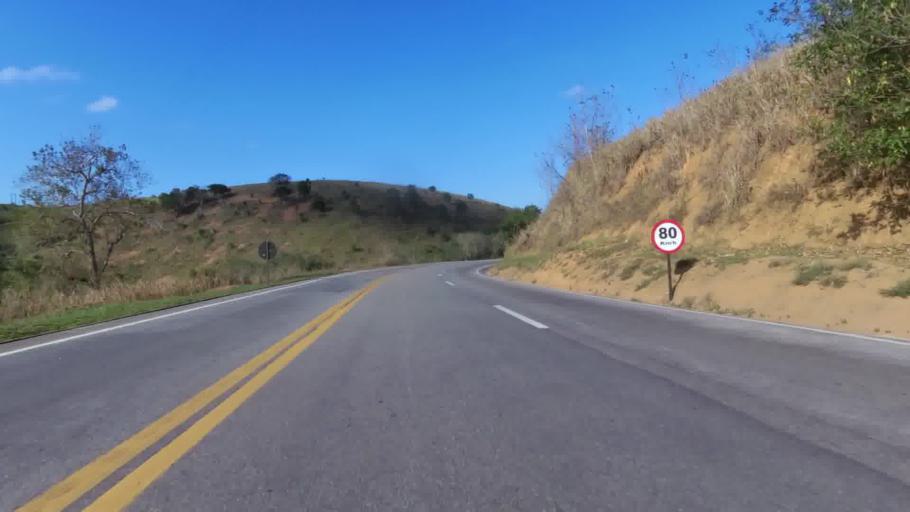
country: BR
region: Espirito Santo
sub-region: Mimoso Do Sul
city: Mimoso do Sul
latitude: -21.2190
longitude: -41.3056
